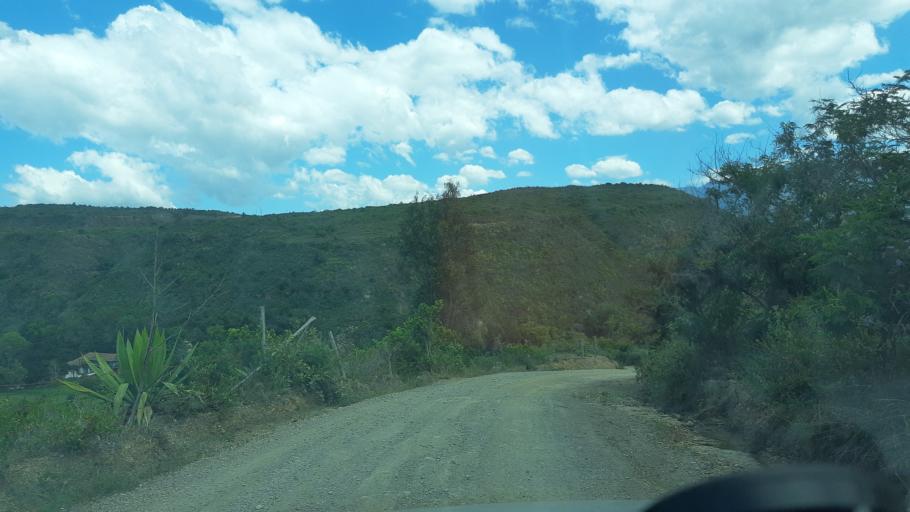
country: CO
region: Boyaca
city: Villa de Leiva
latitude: 5.6769
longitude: -73.5669
